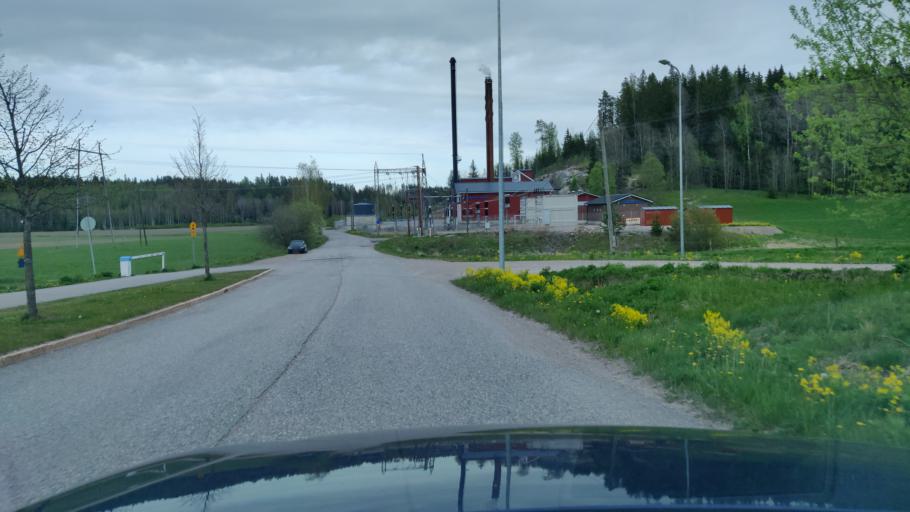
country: FI
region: Uusimaa
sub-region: Helsinki
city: Nurmijaervi
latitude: 60.3844
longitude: 24.7621
